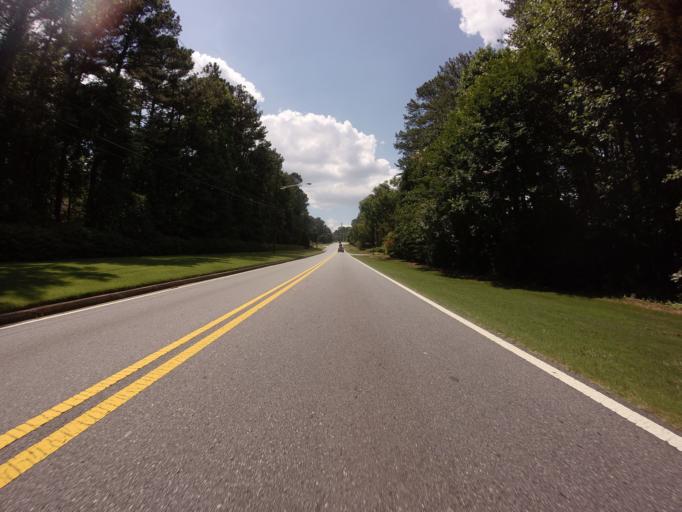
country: US
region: Georgia
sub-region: Fulton County
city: Johns Creek
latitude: 34.0217
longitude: -84.2478
